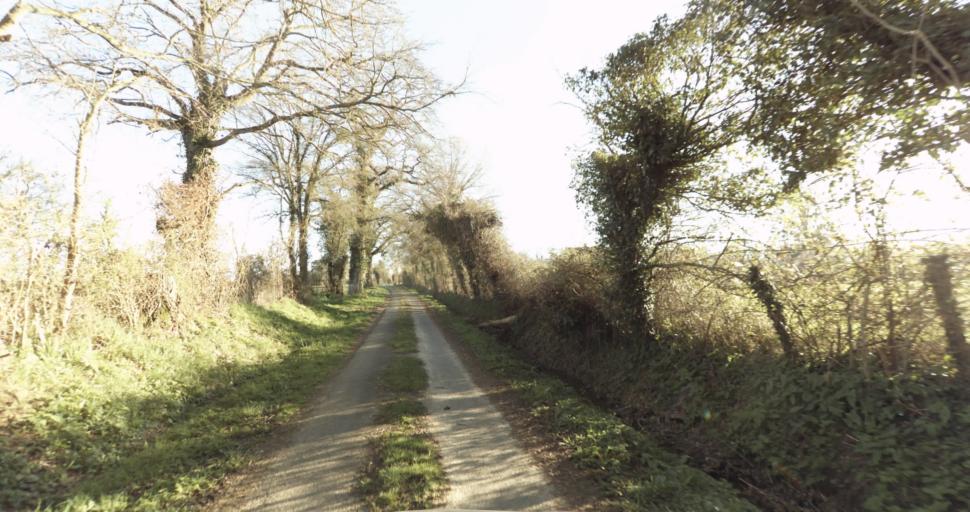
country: FR
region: Lower Normandy
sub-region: Departement de l'Orne
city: Trun
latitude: 48.9094
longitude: 0.0173
